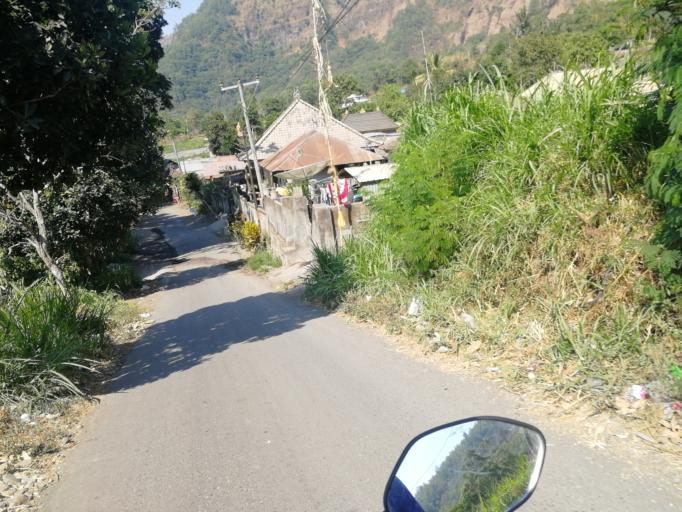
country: ID
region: Bali
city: Banjar Buahan
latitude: -8.2799
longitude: 115.4108
